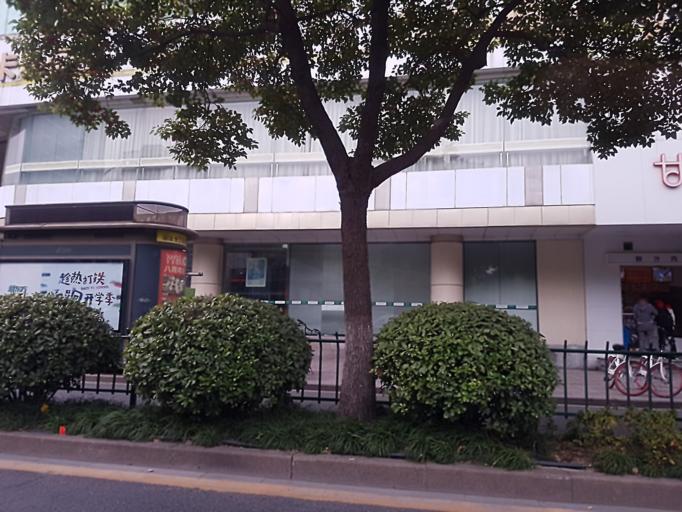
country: CN
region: Zhejiang Sheng
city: Gudang
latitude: 30.2857
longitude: 120.1307
